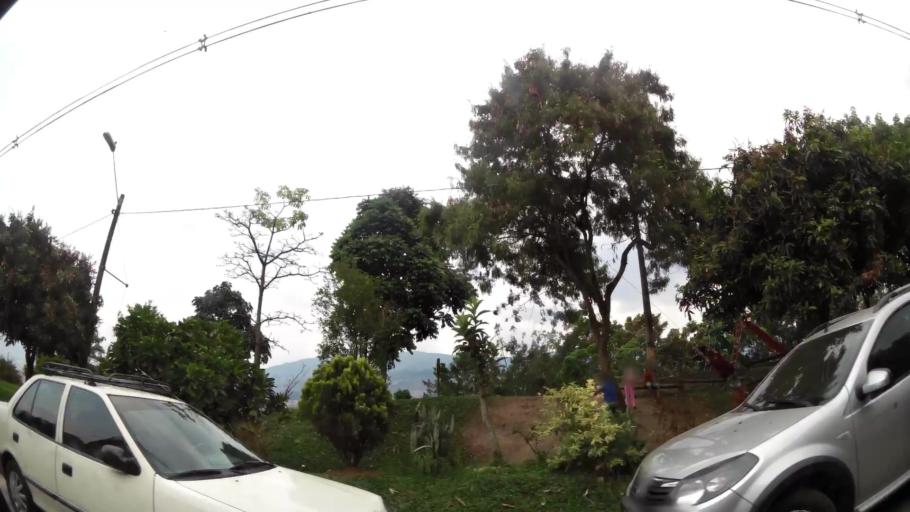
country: CO
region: Antioquia
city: Medellin
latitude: 6.2300
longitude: -75.5535
